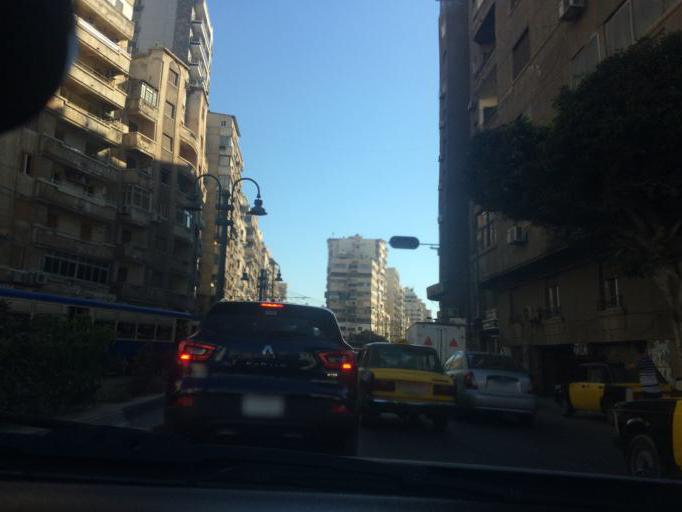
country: EG
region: Alexandria
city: Alexandria
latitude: 31.2324
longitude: 29.9570
